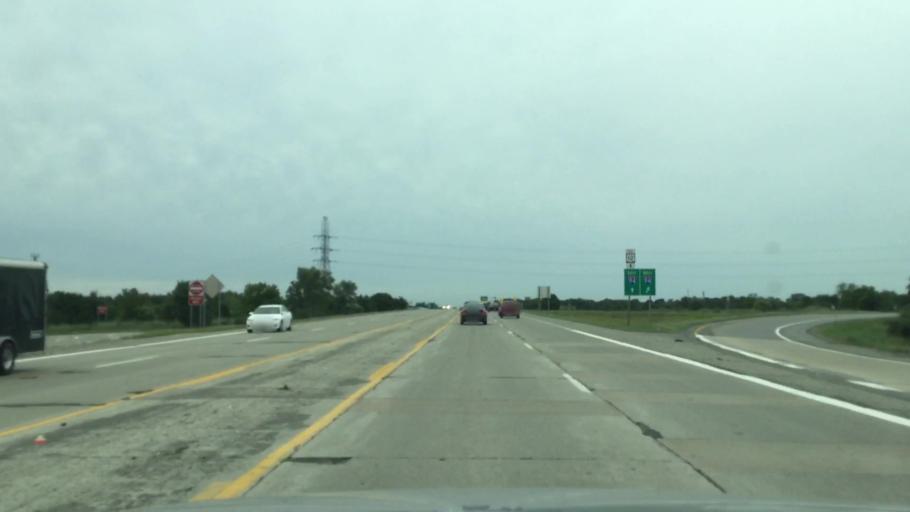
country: US
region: Michigan
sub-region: Washtenaw County
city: Ypsilanti
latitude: 42.2263
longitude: -83.6475
